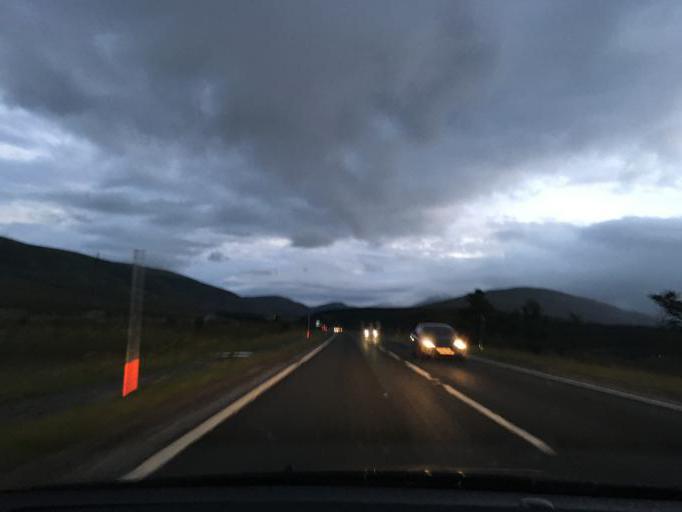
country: GB
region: Scotland
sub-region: Highland
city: Kingussie
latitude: 56.9331
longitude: -4.2342
